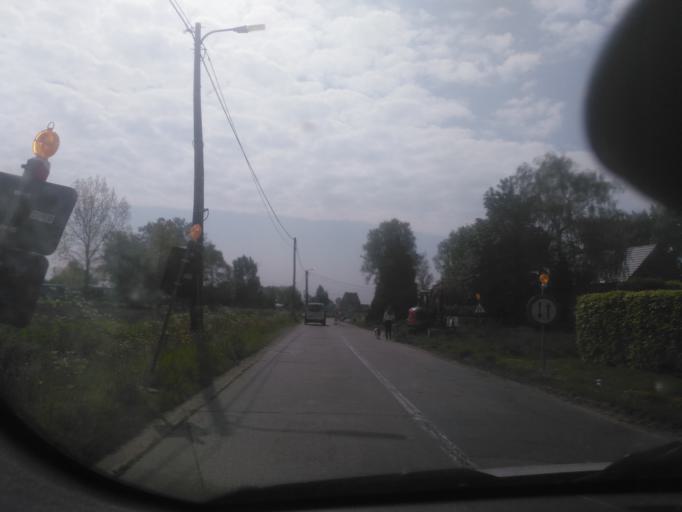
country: BE
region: Flanders
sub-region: Provincie Oost-Vlaanderen
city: Beveren
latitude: 51.2122
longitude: 4.2083
